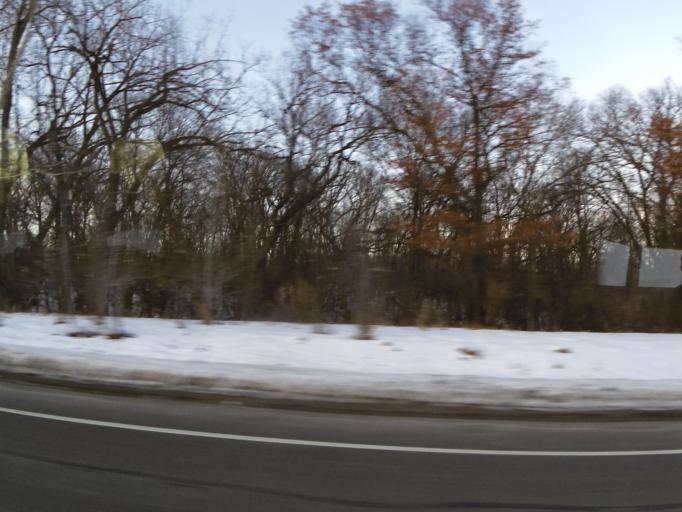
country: US
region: Minnesota
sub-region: Washington County
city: Dellwood
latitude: 45.0970
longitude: -92.9840
